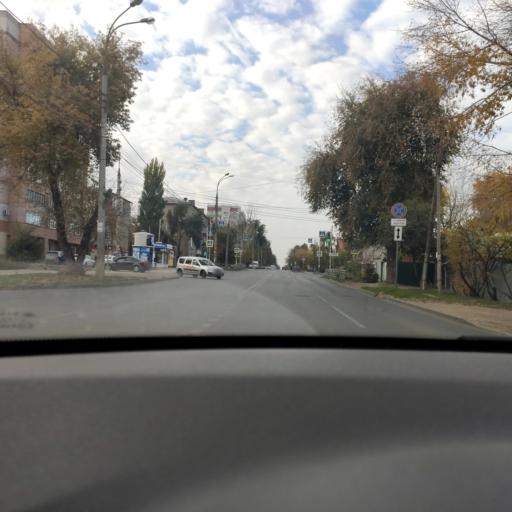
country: RU
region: Samara
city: Samara
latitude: 53.1973
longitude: 50.2001
